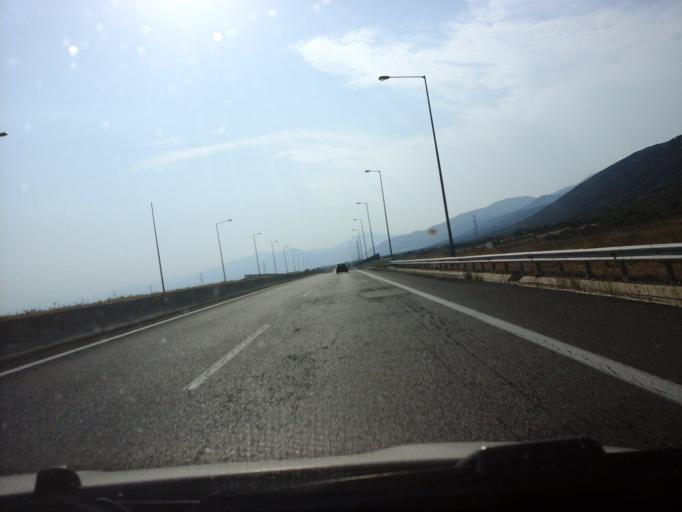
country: GR
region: East Macedonia and Thrace
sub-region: Nomos Rodopis
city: Iasmos
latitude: 41.1157
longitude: 25.1148
